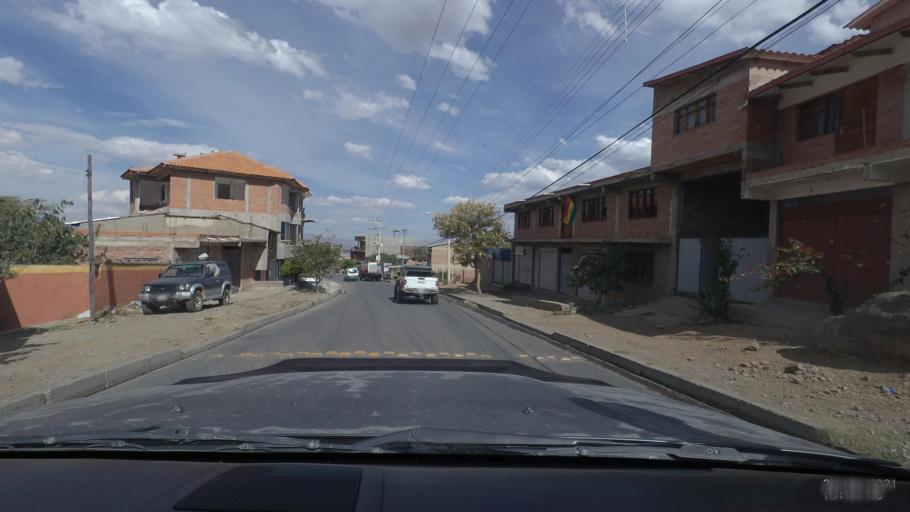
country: BO
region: Cochabamba
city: Cochabamba
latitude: -17.3160
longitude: -66.2843
